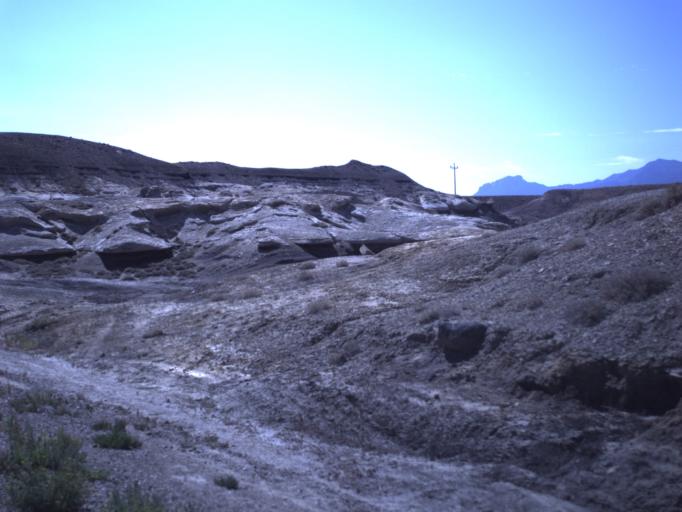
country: US
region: Utah
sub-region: Wayne County
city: Loa
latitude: 38.3661
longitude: -110.9058
